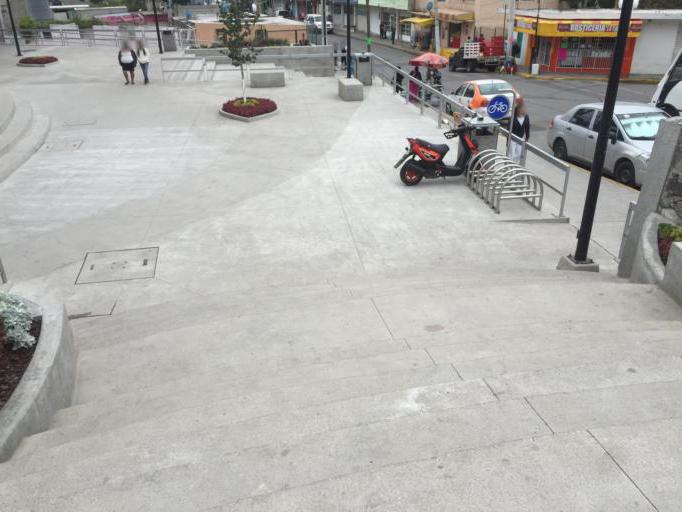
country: MX
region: Mexico
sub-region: Tlalnepantla de Baz
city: Puerto Escondido (Tepeolulco Puerto Escondido)
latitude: 19.5687
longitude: -99.0922
